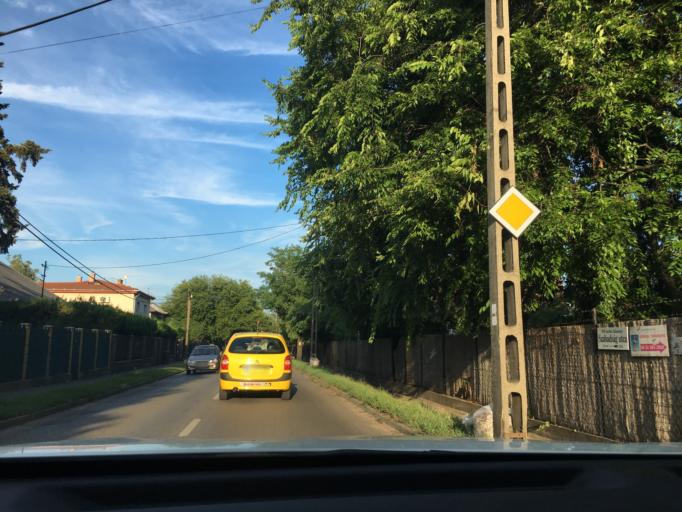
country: HU
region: Budapest
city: Budapest XVII. keruelet
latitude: 47.4678
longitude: 19.2452
